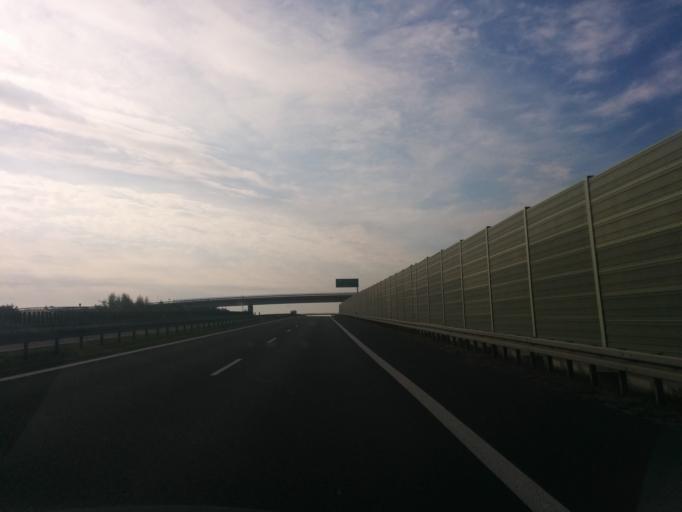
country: PL
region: Masovian Voivodeship
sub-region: Powiat grojecki
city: Jasieniec
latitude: 51.7883
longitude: 20.8935
